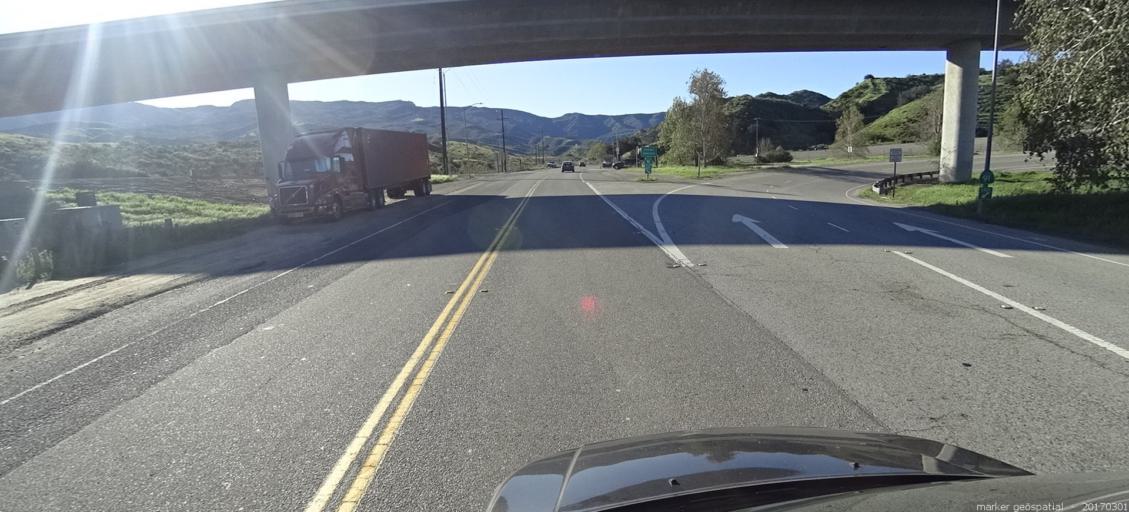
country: US
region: California
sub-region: Orange County
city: Yorba Linda
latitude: 33.8665
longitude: -117.7114
